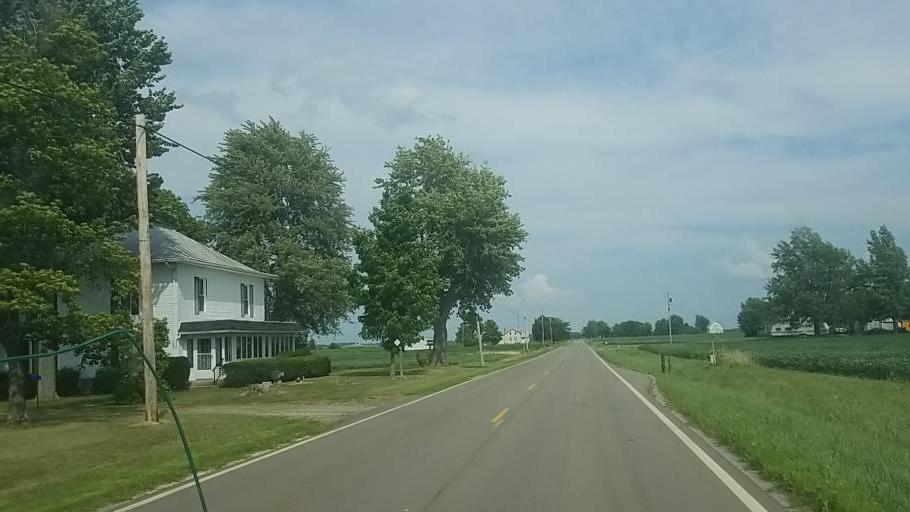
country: US
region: Ohio
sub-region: Hardin County
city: Forest
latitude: 40.8036
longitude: -83.4789
